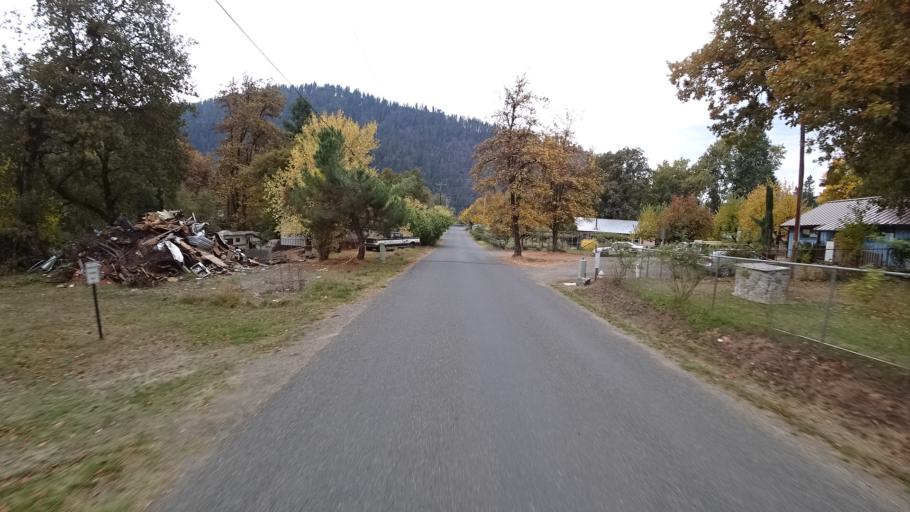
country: US
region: California
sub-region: Siskiyou County
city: Happy Camp
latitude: 41.7943
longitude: -123.3799
